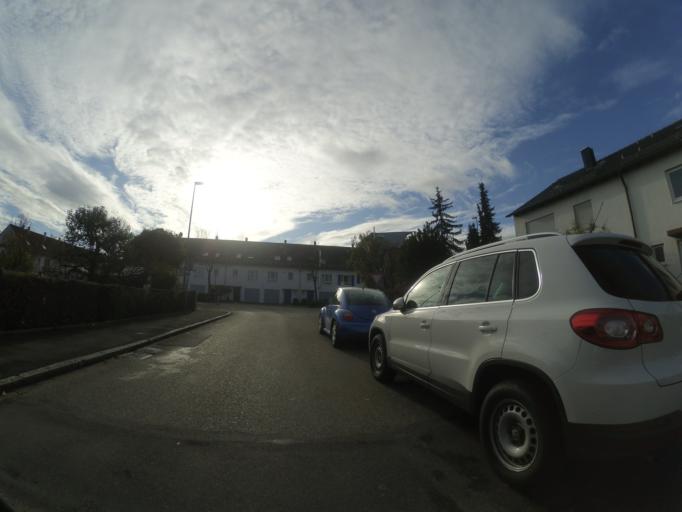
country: DE
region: Bavaria
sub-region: Swabia
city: Neu-Ulm
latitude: 48.4042
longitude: 10.0250
